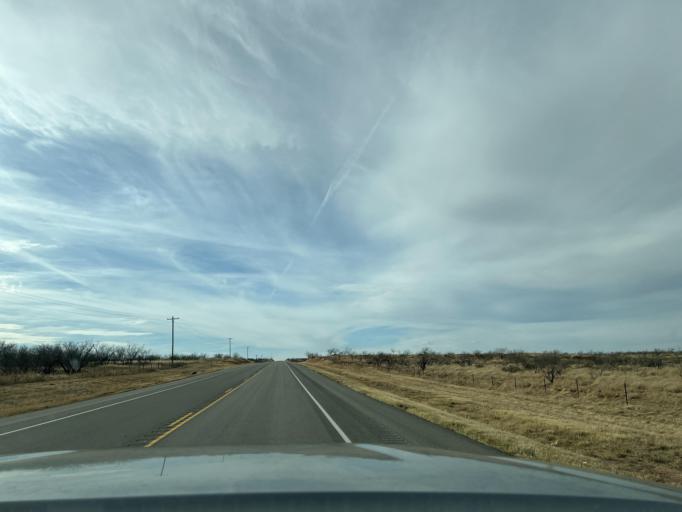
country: US
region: Texas
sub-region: Jones County
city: Anson
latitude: 32.7508
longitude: -99.7342
